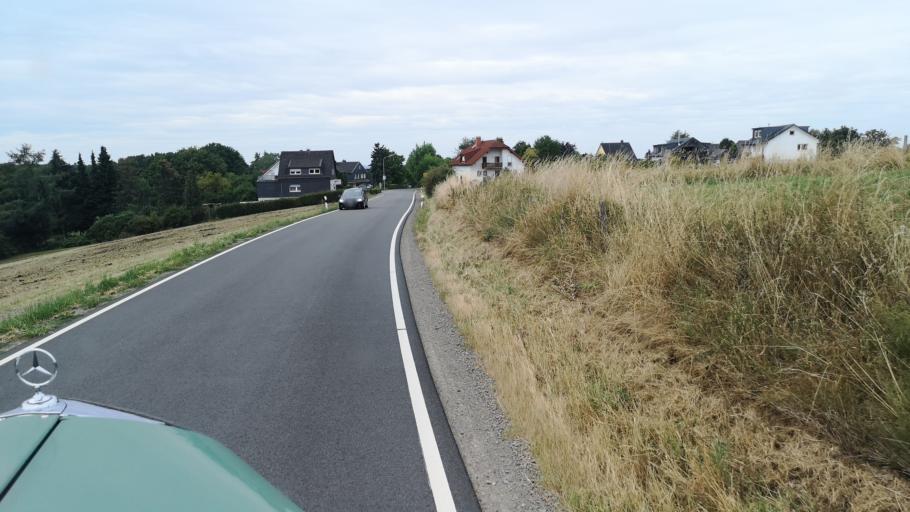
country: DE
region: North Rhine-Westphalia
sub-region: Regierungsbezirk Koln
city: Odenthal
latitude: 51.0587
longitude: 7.1619
